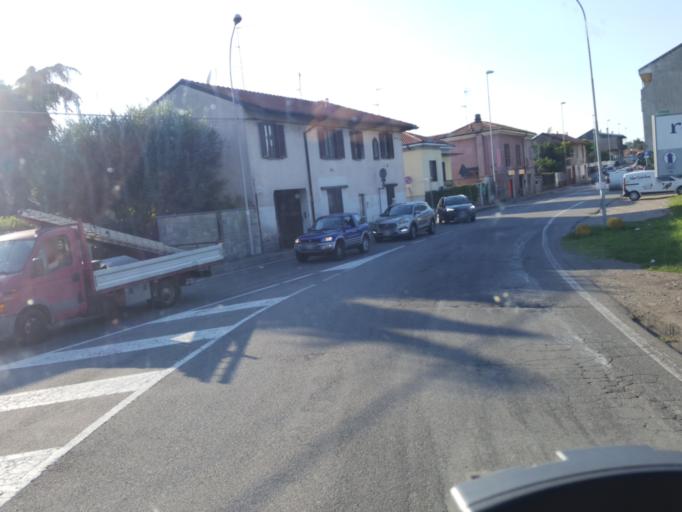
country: IT
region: Lombardy
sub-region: Citta metropolitana di Milano
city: Parabiago
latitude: 45.5519
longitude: 8.9558
